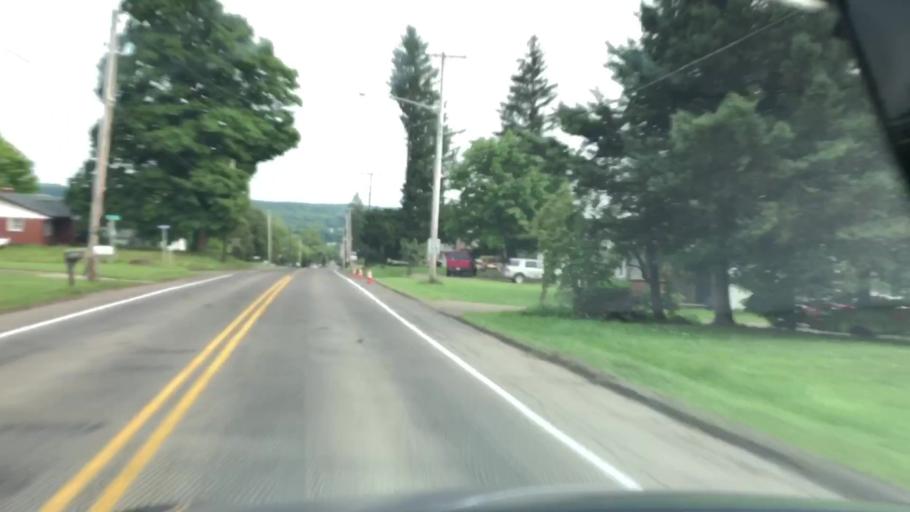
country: US
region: Pennsylvania
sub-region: Crawford County
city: Titusville
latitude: 41.7434
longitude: -79.7659
